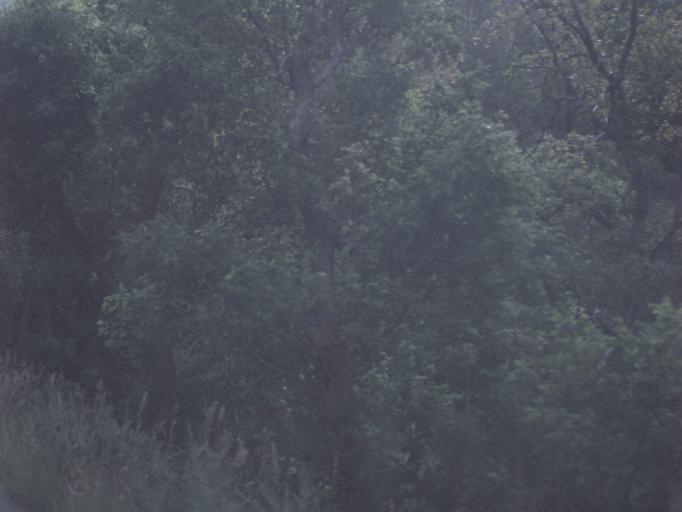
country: US
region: Utah
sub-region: Utah County
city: Cedar Hills
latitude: 40.4405
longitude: -111.7180
